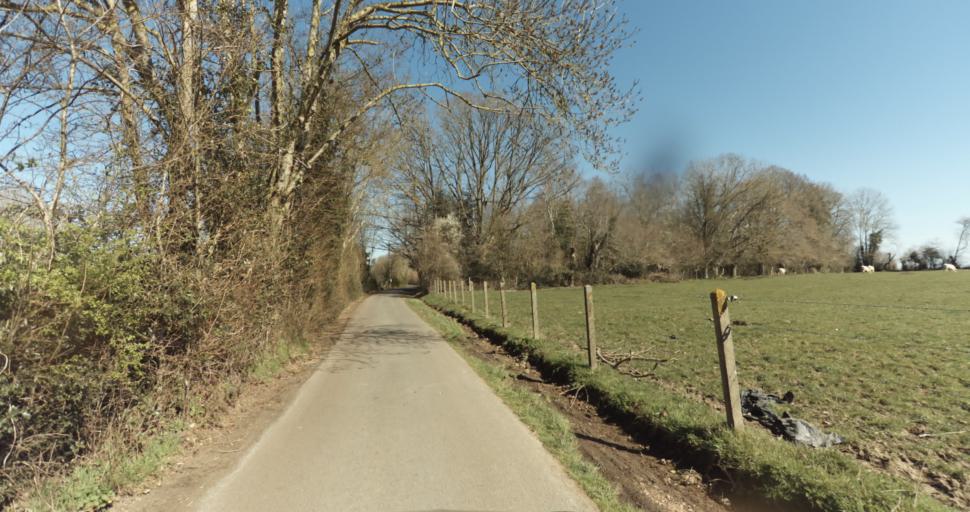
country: FR
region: Lower Normandy
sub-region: Departement du Calvados
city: Livarot
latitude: 48.9754
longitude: 0.0957
